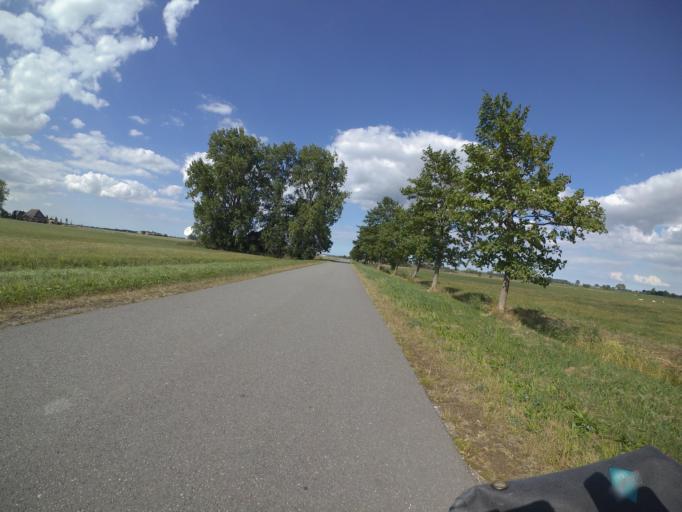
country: NL
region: Friesland
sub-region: Gemeente Kollumerland en Nieuwkruisland
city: Kollum
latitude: 53.2766
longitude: 6.2235
